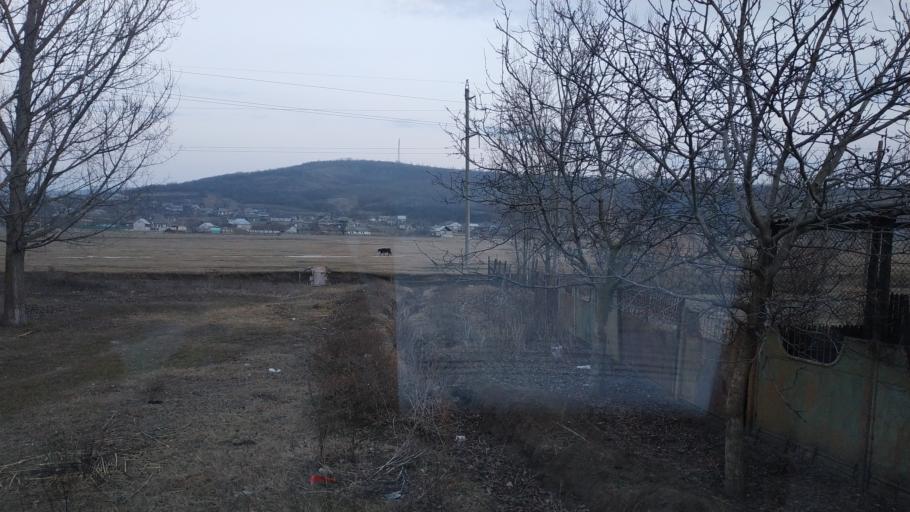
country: RO
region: Vaslui
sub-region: Comuna Stanilesti
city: Stanilesti
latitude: 46.6580
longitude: 28.3066
